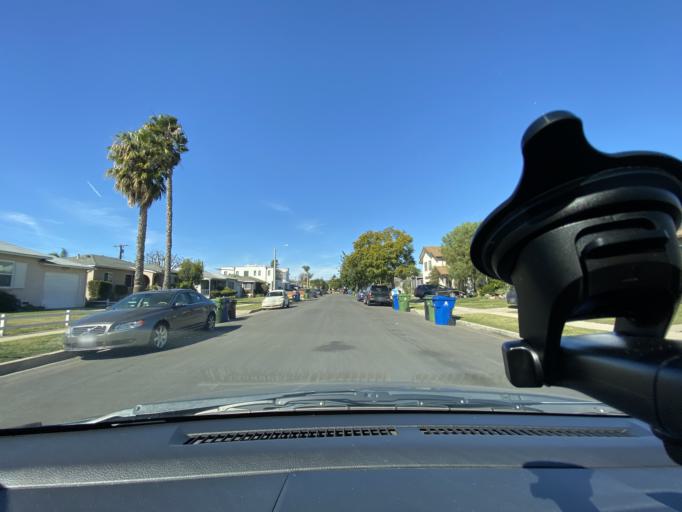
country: US
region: California
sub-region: Los Angeles County
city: Westwood, Los Angeles
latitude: 34.0253
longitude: -118.4385
